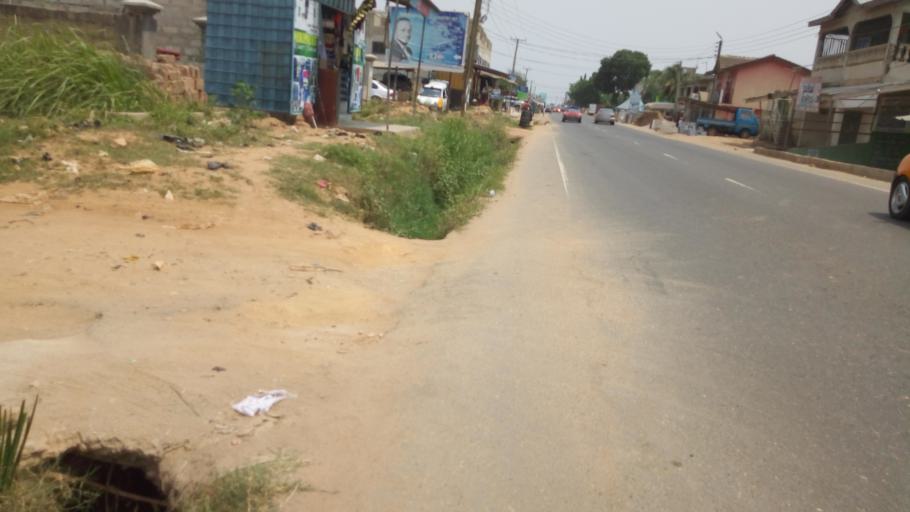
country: GH
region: Greater Accra
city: Gbawe
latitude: 5.5575
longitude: -0.3065
